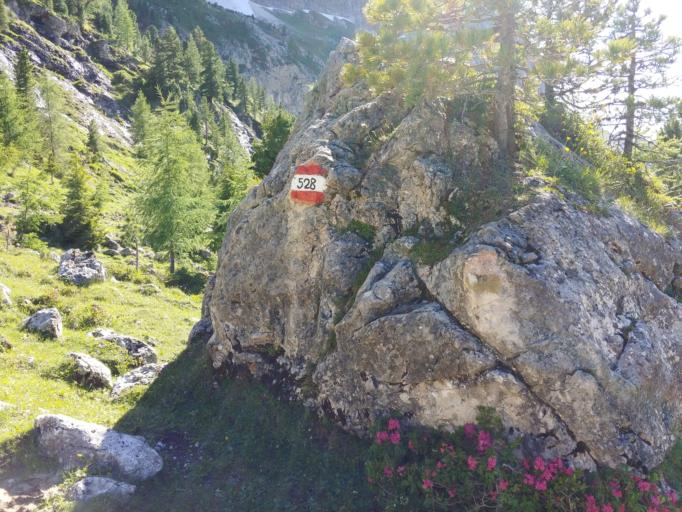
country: IT
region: Trentino-Alto Adige
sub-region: Bolzano
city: Selva
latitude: 46.5309
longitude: 11.7437
